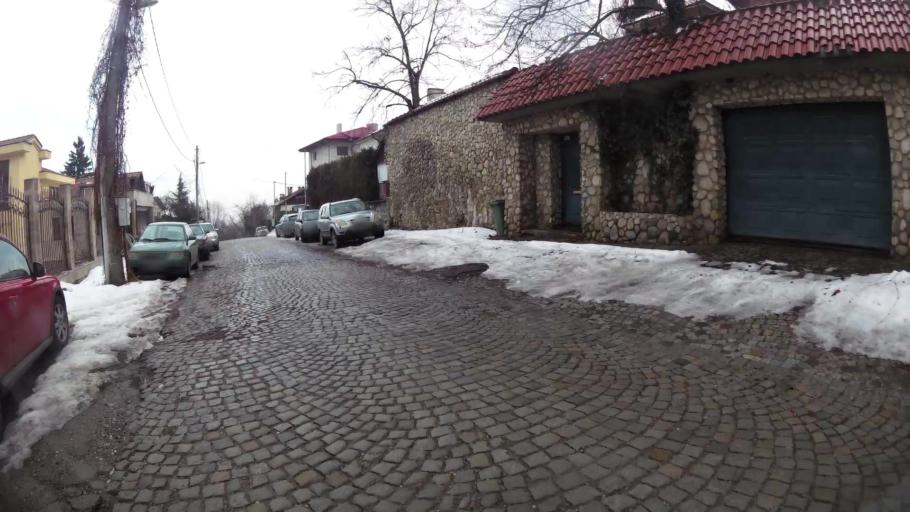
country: BG
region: Sofia-Capital
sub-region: Stolichna Obshtina
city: Sofia
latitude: 42.6456
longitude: 23.2642
